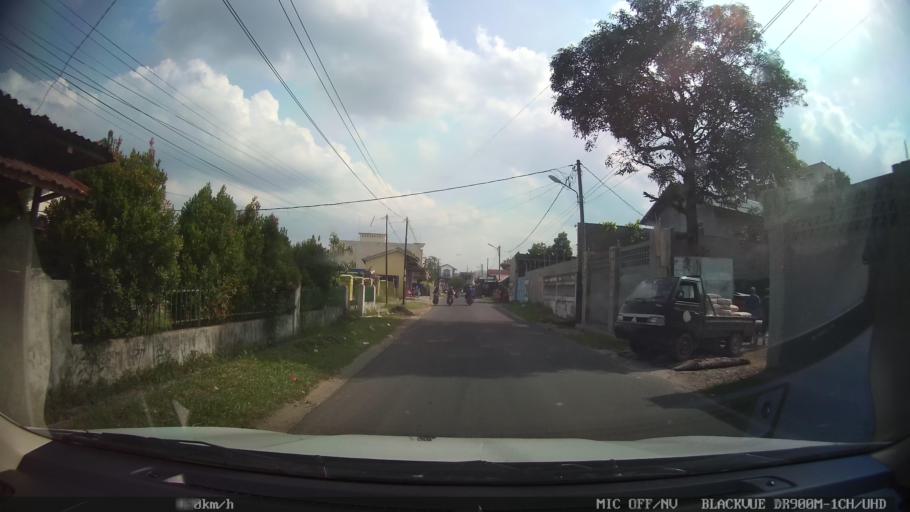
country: ID
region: North Sumatra
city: Binjai
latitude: 3.6116
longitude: 98.4983
